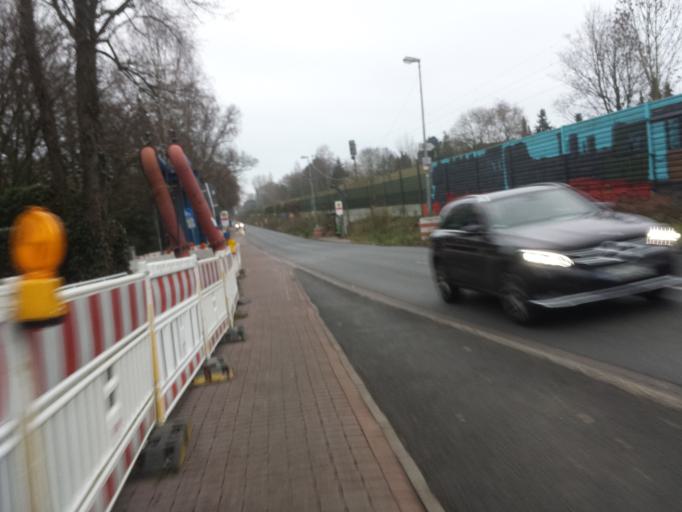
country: DE
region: Bremen
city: Bremen
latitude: 53.0994
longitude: 8.8620
